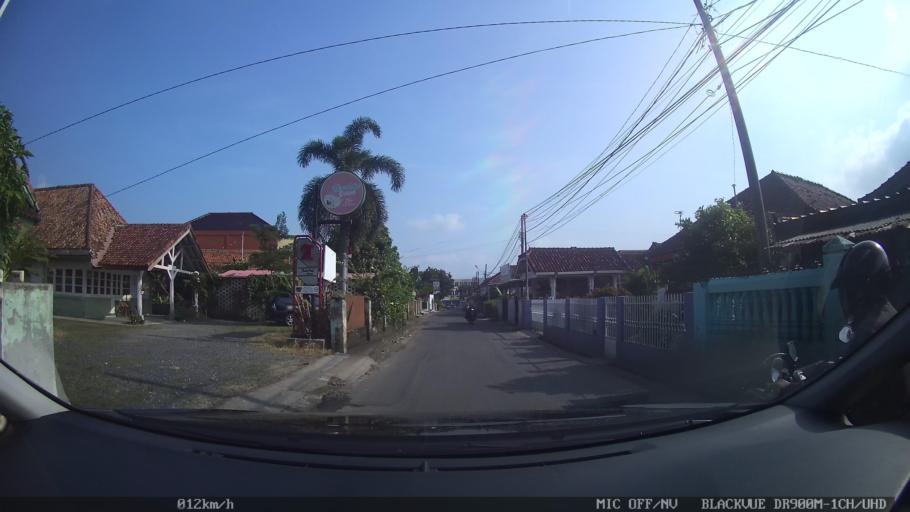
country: ID
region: Lampung
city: Kedaton
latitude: -5.3884
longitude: 105.2637
